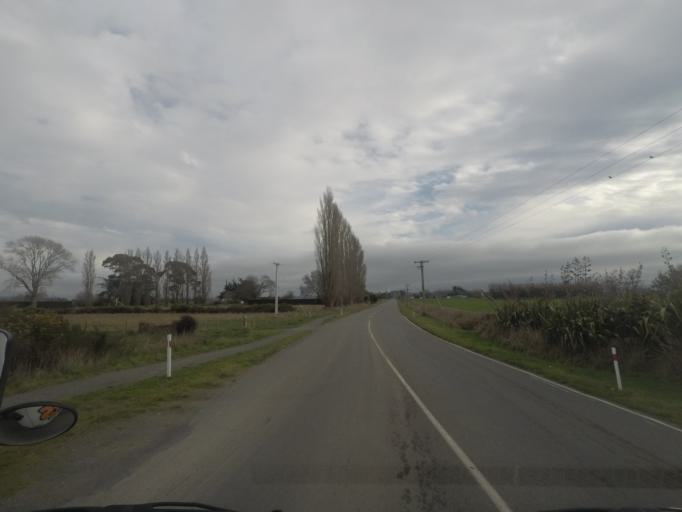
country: NZ
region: Canterbury
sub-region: Waimakariri District
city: Woodend
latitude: -43.2905
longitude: 172.6992
